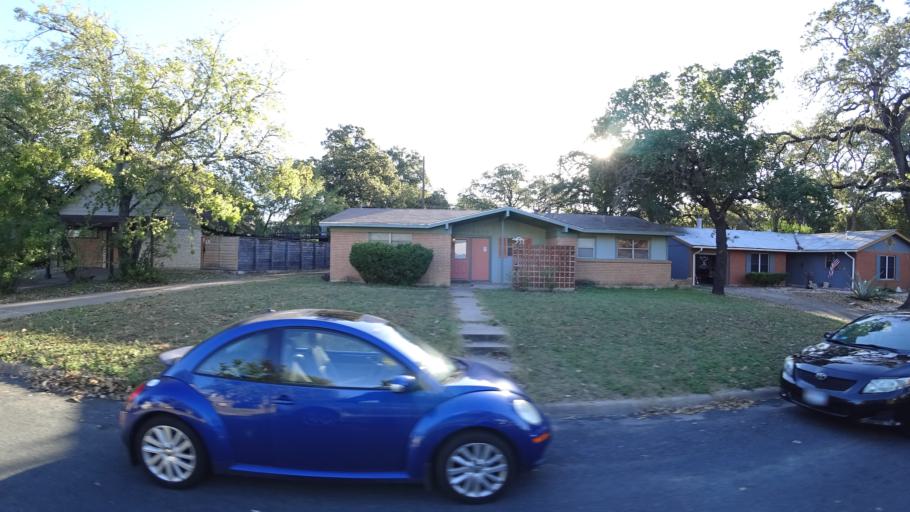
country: US
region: Texas
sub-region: Travis County
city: Austin
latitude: 30.3055
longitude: -97.6846
